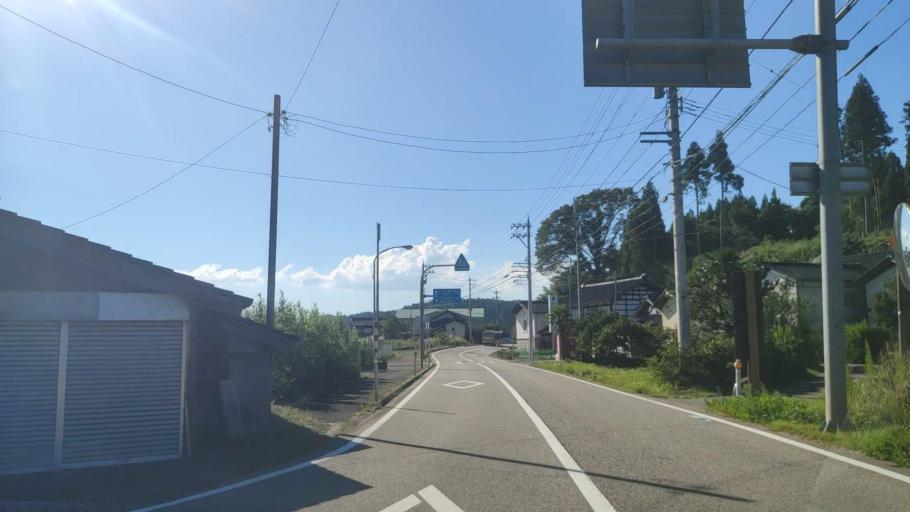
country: JP
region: Ishikawa
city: Nanao
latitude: 37.2350
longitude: 136.9668
